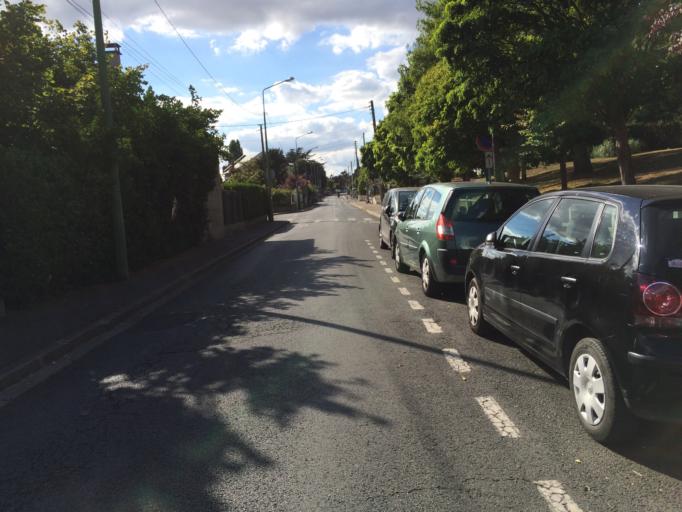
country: FR
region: Ile-de-France
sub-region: Departement de l'Essonne
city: Villebon-sur-Yvette
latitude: 48.7037
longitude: 2.2200
